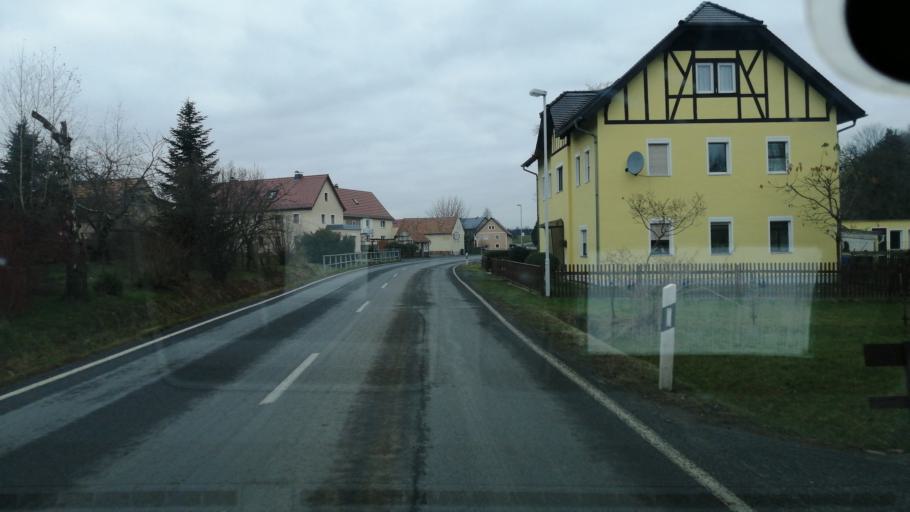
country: DE
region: Saxony
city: Sohland am Rotstein
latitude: 51.0690
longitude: 14.7808
